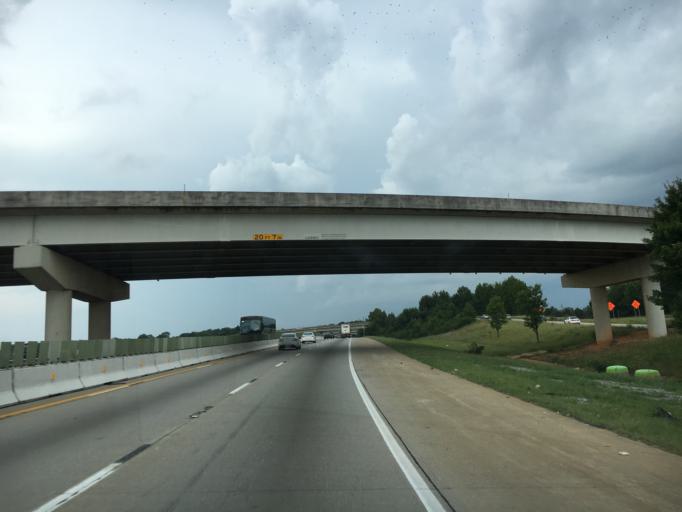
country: US
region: South Carolina
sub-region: Spartanburg County
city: Southern Shops
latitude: 34.9794
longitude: -82.0069
